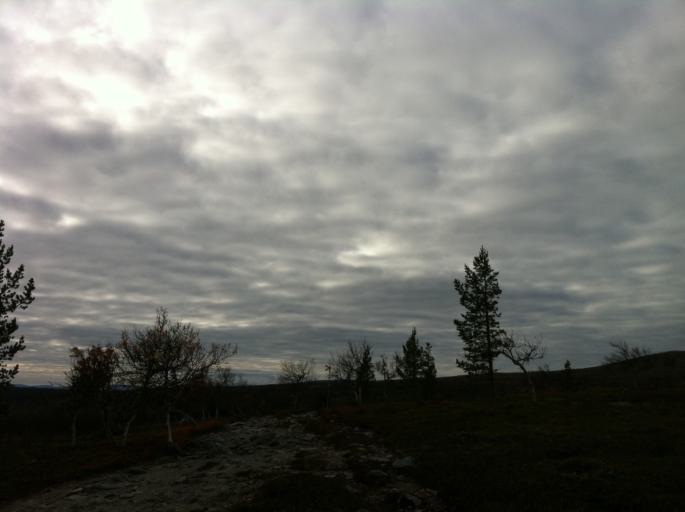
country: NO
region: Hedmark
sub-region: Engerdal
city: Engerdal
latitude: 62.0982
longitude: 12.2666
